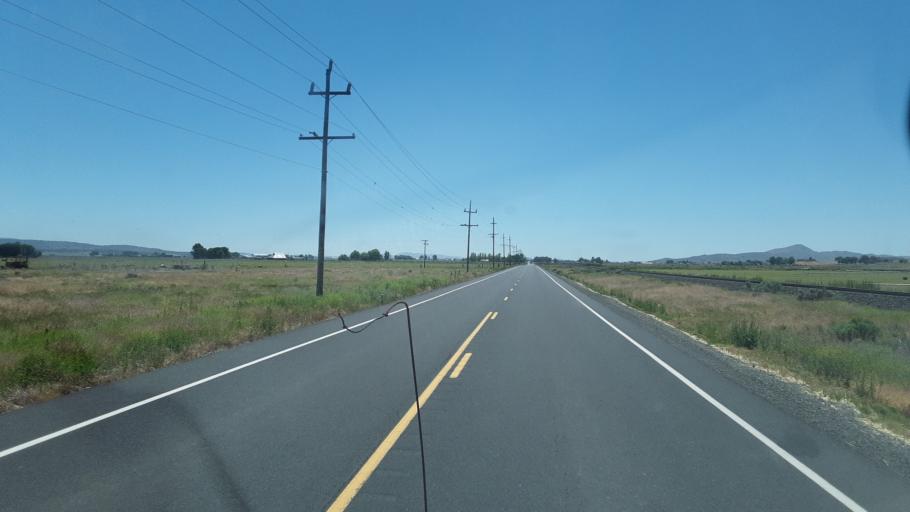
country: US
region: Oregon
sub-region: Klamath County
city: Altamont
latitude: 42.0605
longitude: -121.6518
